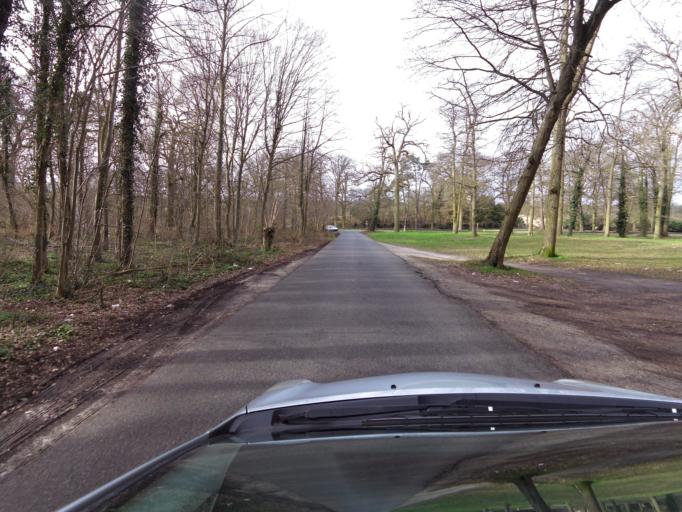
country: FR
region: Picardie
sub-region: Departement de l'Oise
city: Ver-sur-Launette
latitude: 49.1458
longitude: 2.6814
